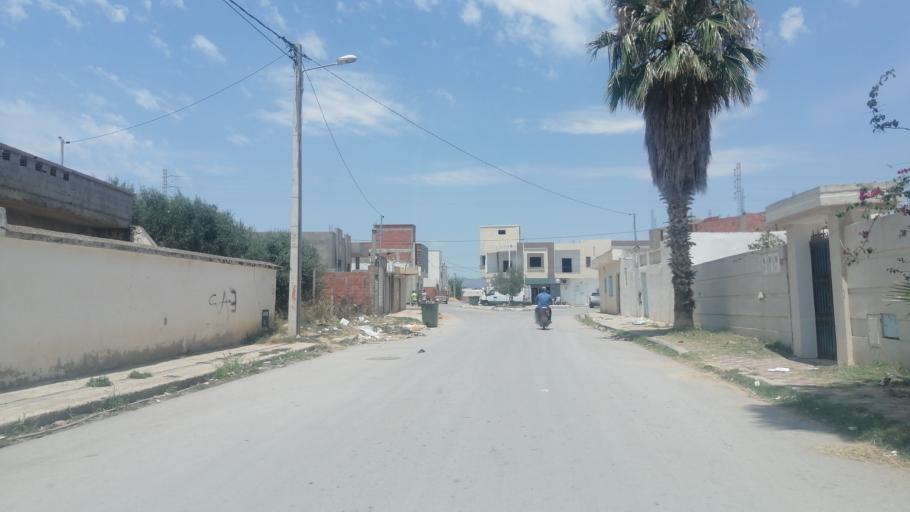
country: TN
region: Al Qayrawan
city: Sbikha
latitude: 36.1225
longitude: 10.0919
